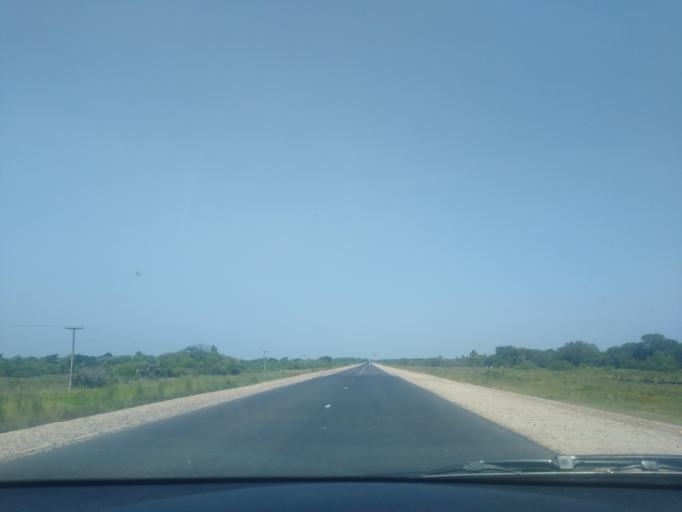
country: AR
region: Chaco
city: Puerto Tirol
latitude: -27.5699
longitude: -59.2711
